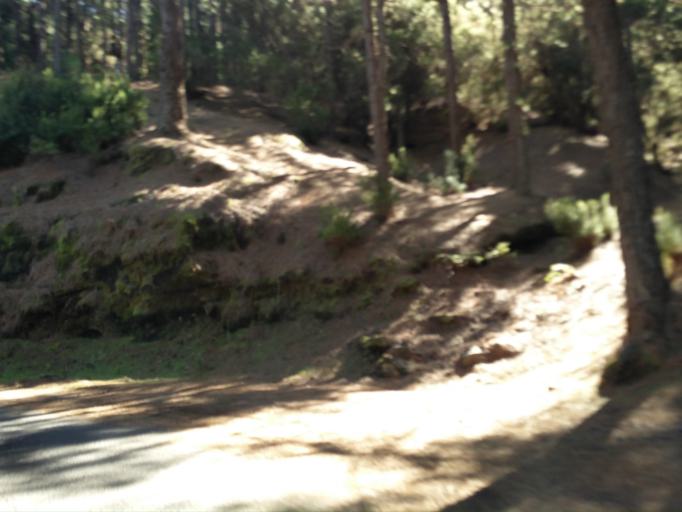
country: ES
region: Canary Islands
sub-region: Provincia de Santa Cruz de Tenerife
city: Brena Baja
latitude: 28.6131
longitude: -17.8405
